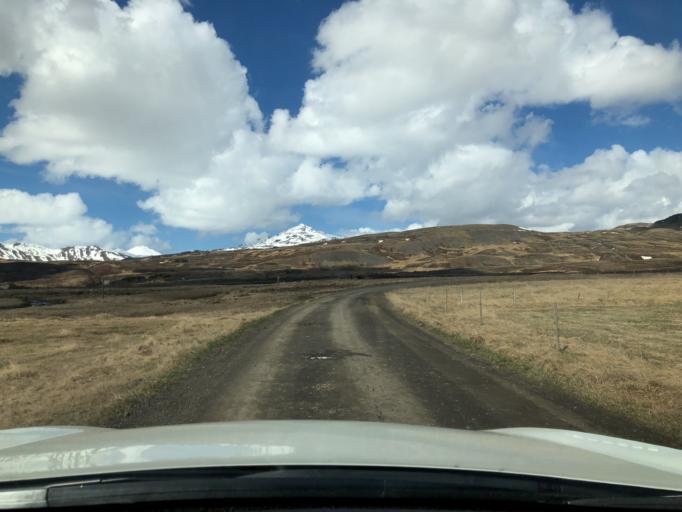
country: IS
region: West
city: Stykkisholmur
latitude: 64.8532
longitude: -22.3727
